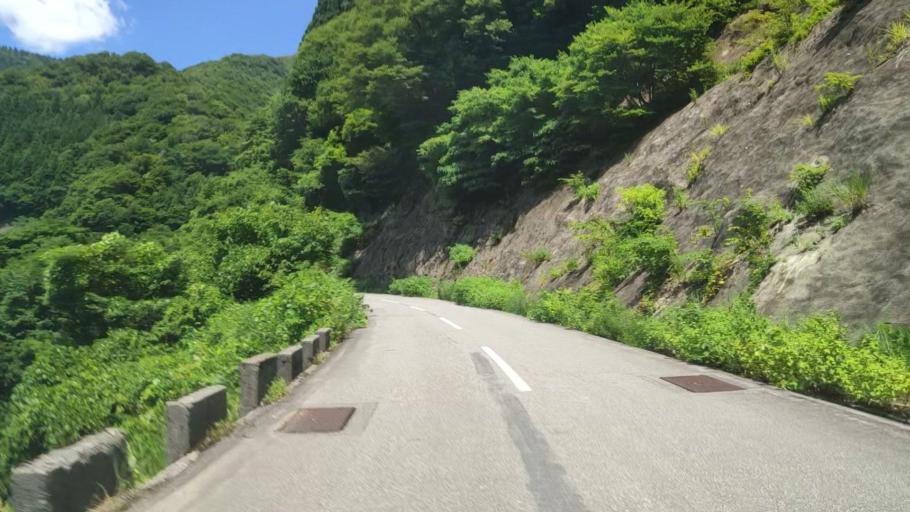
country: JP
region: Fukui
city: Ono
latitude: 35.8996
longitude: 136.5181
